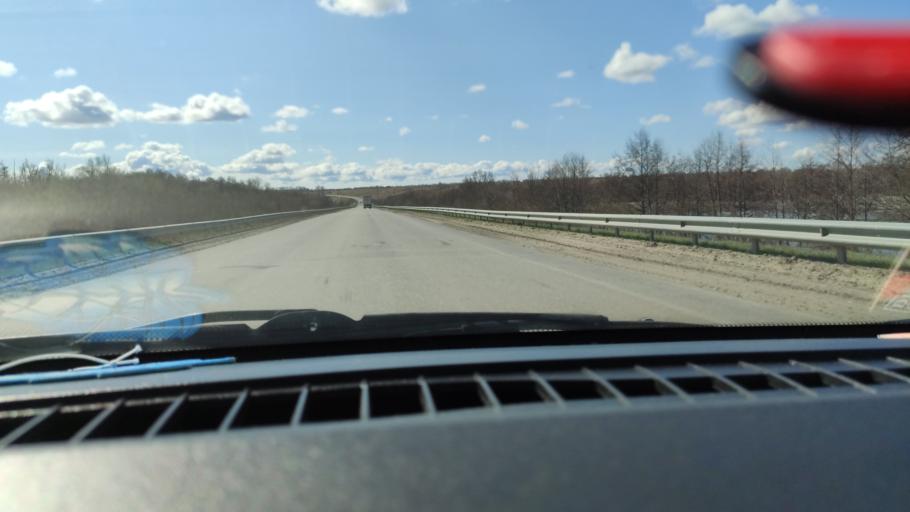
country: RU
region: Samara
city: Varlamovo
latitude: 53.1323
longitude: 48.2868
